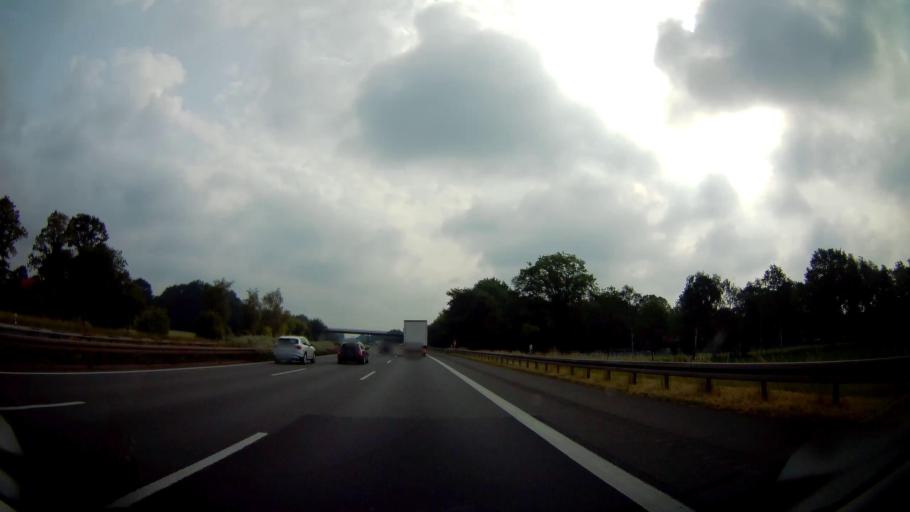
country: DE
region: North Rhine-Westphalia
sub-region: Regierungsbezirk Detmold
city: Guetersloh
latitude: 51.8735
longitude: 8.4146
